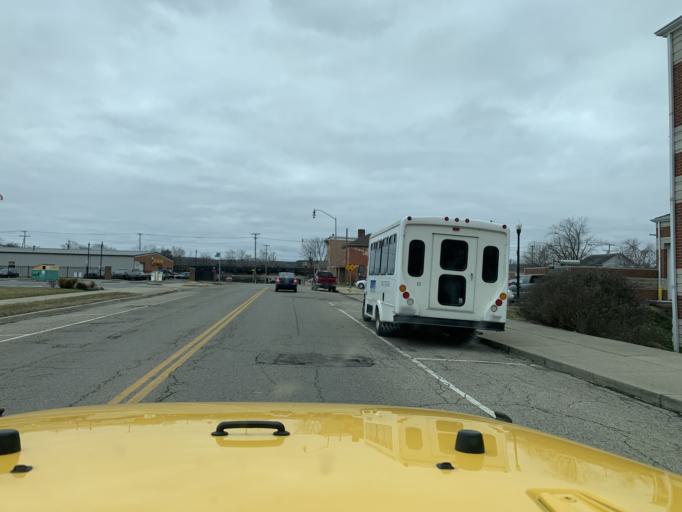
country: US
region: Ohio
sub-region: Licking County
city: Newark
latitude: 40.0561
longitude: -82.4056
